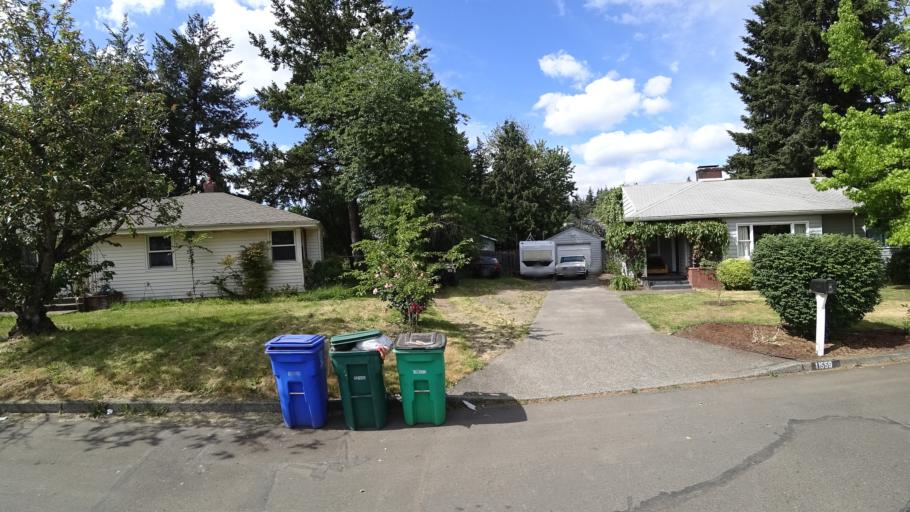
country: US
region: Oregon
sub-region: Multnomah County
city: Lents
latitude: 45.4959
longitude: -122.5438
